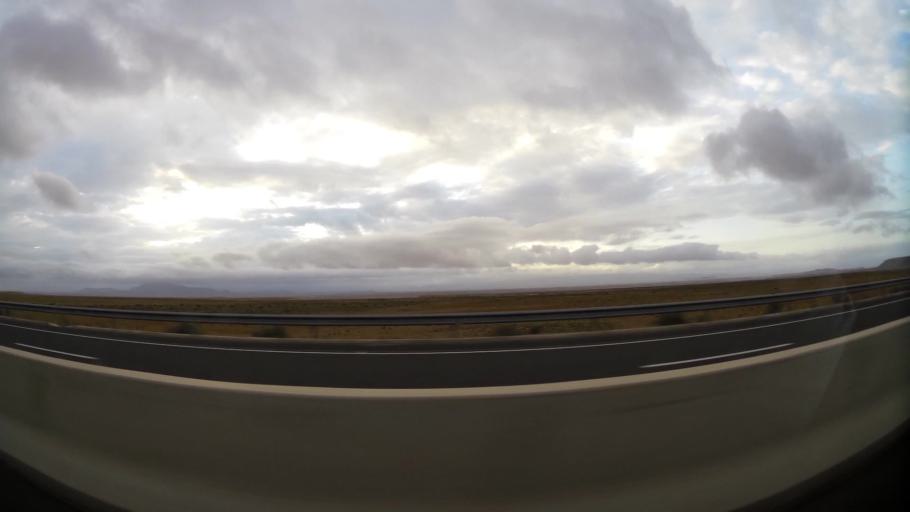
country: MA
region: Oriental
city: Taourirt
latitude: 34.4267
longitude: -3.1013
